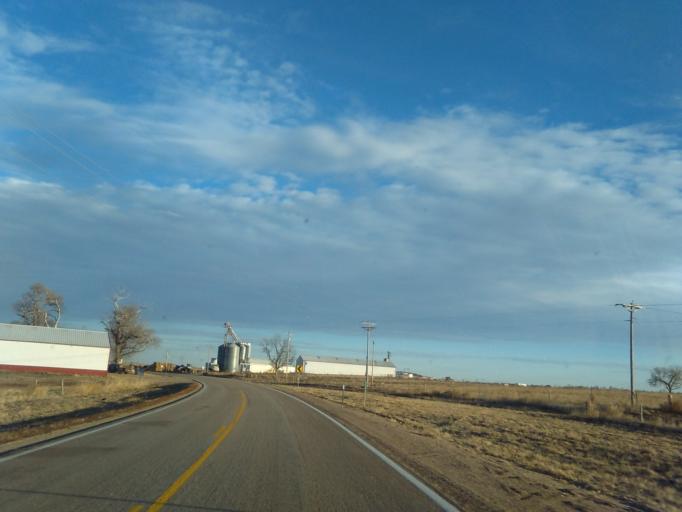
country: US
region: Nebraska
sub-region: Morrill County
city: Bridgeport
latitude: 41.5985
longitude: -102.9767
